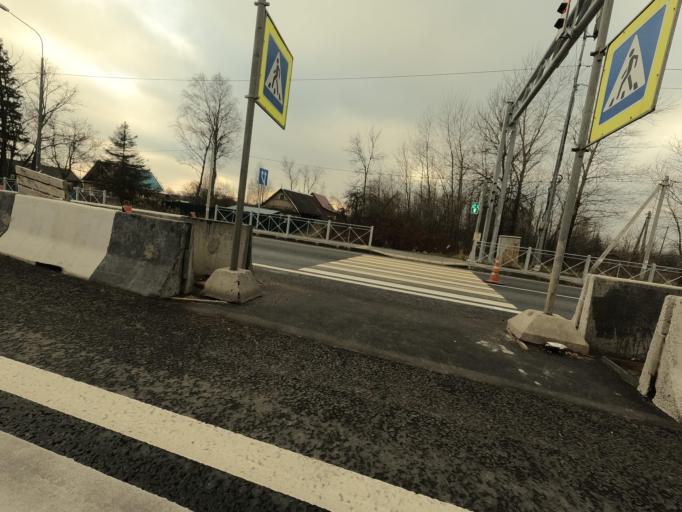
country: RU
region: Leningrad
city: Mga
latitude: 59.7181
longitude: 31.1077
